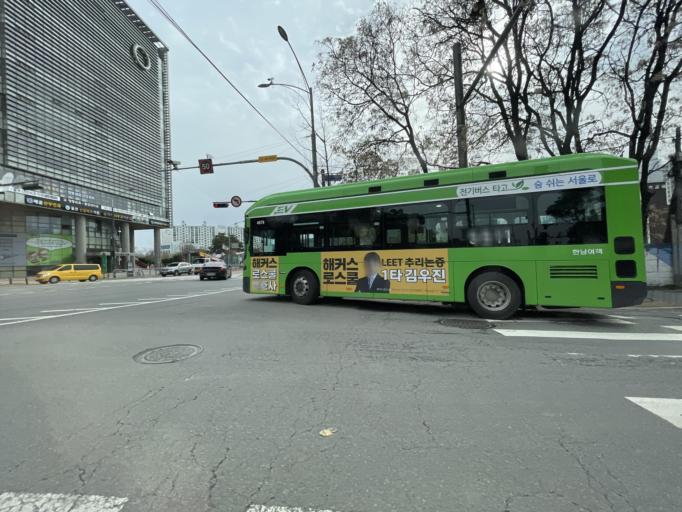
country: KR
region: Seoul
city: Seoul
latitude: 37.5095
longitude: 126.9630
